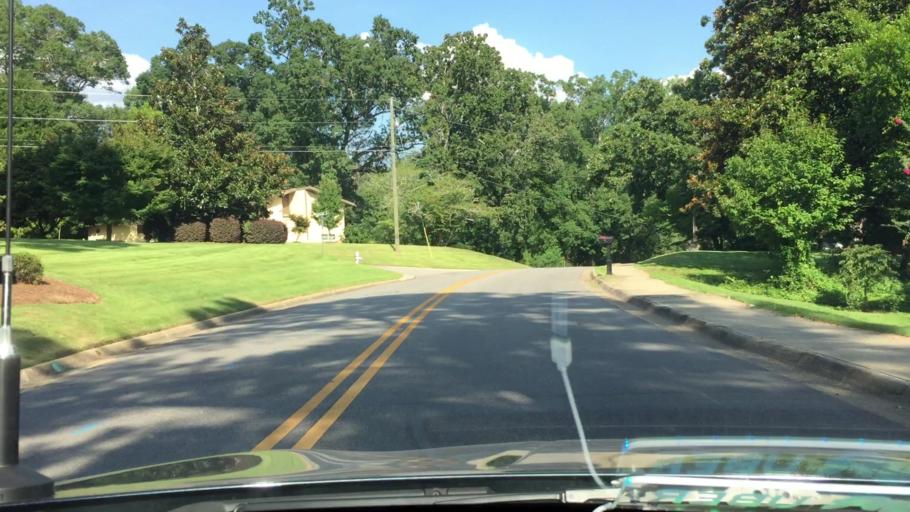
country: US
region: Alabama
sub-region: Lee County
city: Auburn
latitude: 32.6014
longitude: -85.4730
